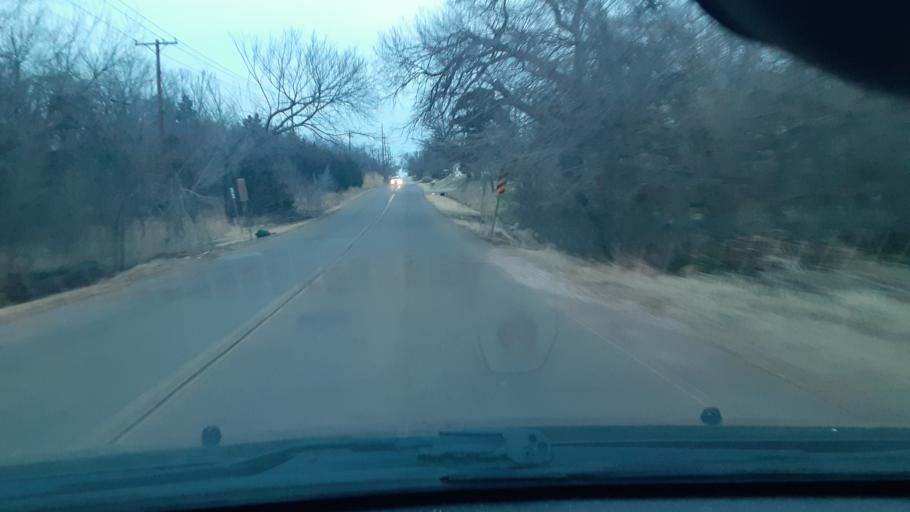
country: US
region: Oklahoma
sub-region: Logan County
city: Guthrie
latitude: 35.8688
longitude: -97.4075
